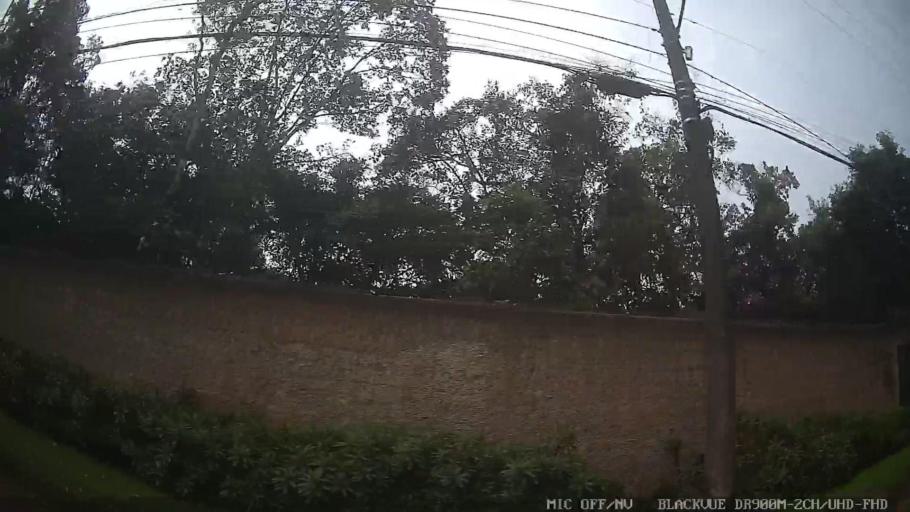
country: BR
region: Sao Paulo
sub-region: Ribeirao Pires
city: Ribeirao Pires
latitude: -23.6824
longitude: -46.3445
